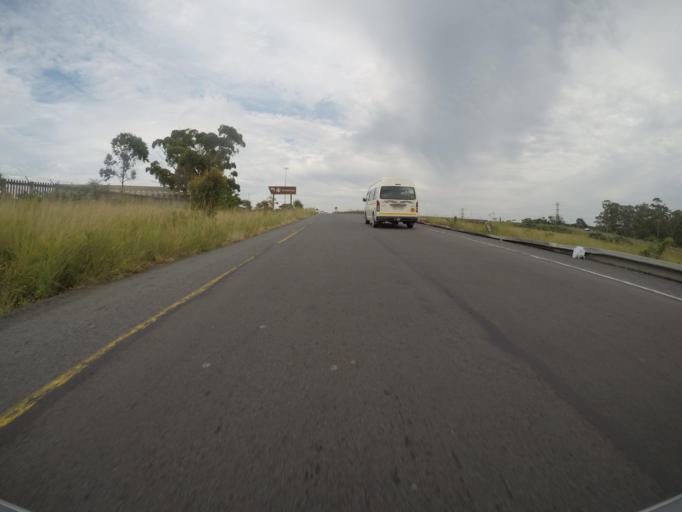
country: ZA
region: Eastern Cape
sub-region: Buffalo City Metropolitan Municipality
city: East London
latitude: -32.9710
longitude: 27.8523
